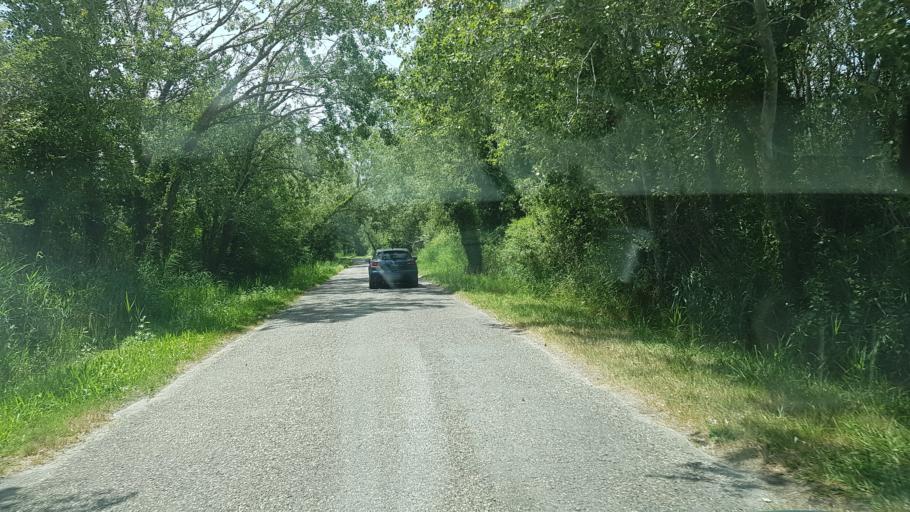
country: FR
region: Provence-Alpes-Cote d'Azur
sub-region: Departement des Bouches-du-Rhone
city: Arles
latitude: 43.5664
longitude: 4.6247
